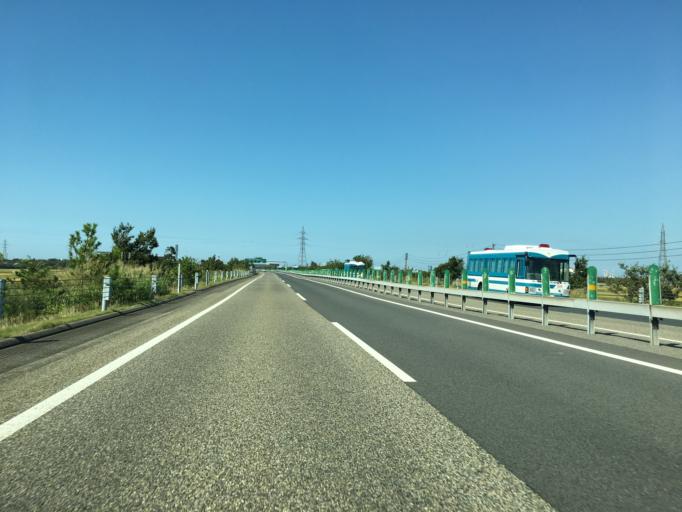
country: JP
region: Niigata
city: Niigata-shi
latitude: 37.8603
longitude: 139.0518
